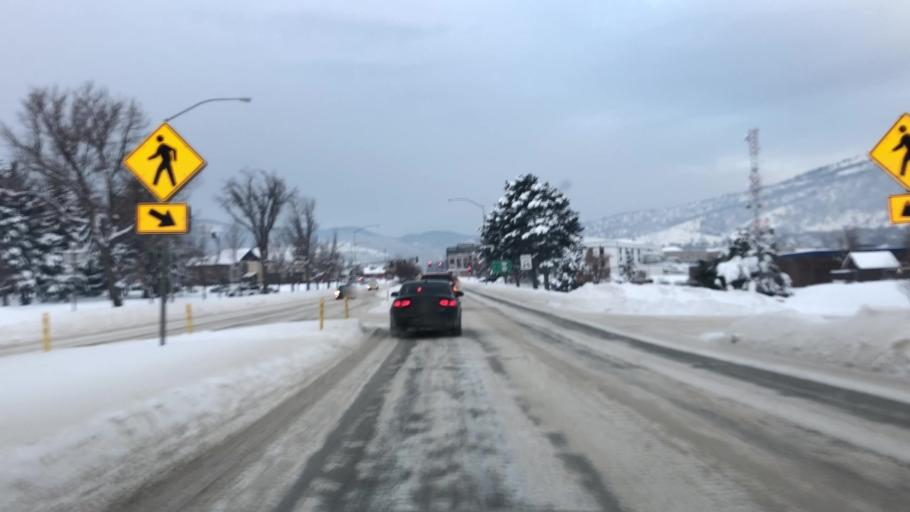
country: US
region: Montana
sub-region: Lewis and Clark County
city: Helena
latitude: 46.6002
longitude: -112.0302
